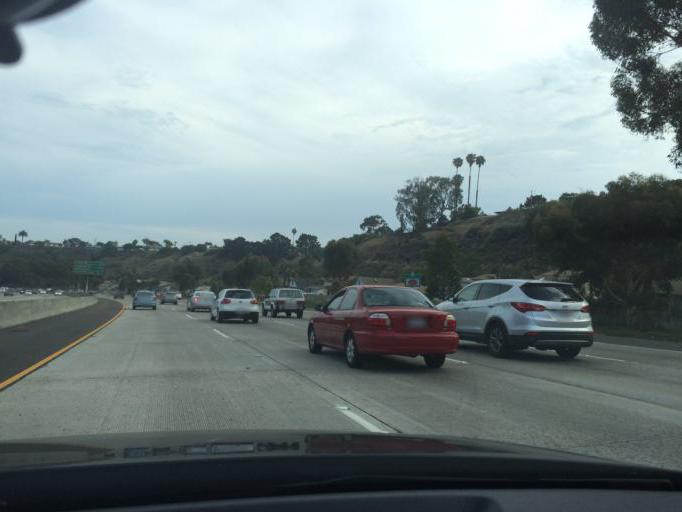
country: US
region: California
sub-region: San Diego County
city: San Diego
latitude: 32.7813
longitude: -117.1629
